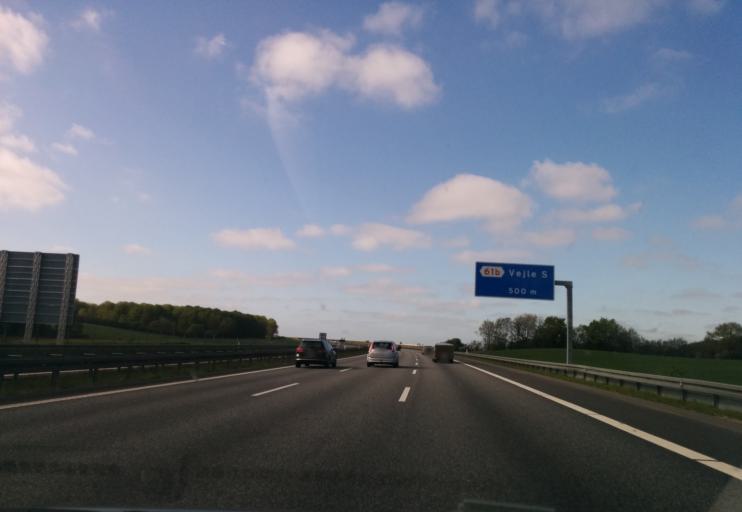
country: DK
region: South Denmark
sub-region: Vejle Kommune
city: Vejle
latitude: 55.6542
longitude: 9.5610
